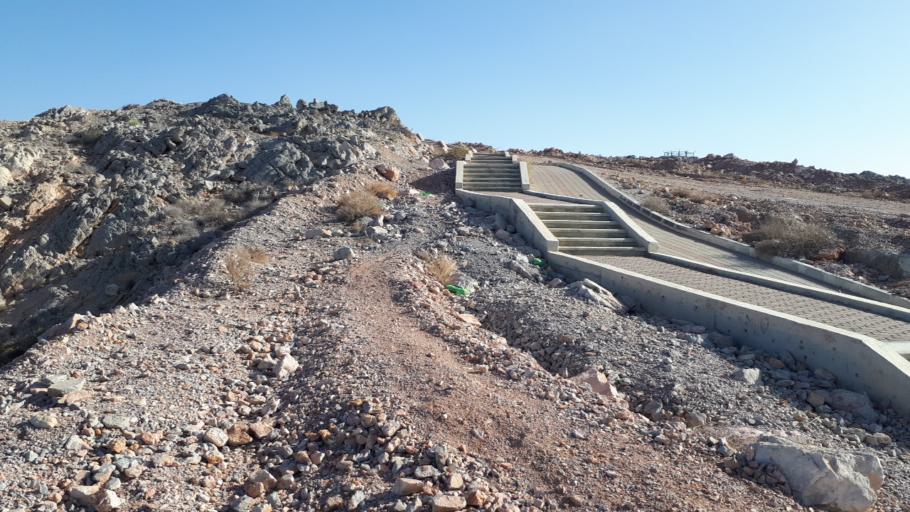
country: OM
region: Muhafazat Masqat
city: Muscat
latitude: 23.5633
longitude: 58.5728
